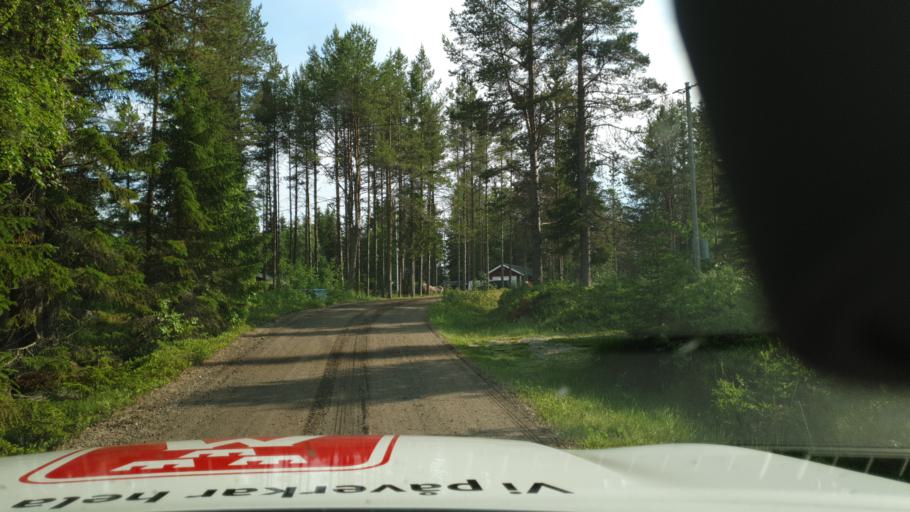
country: SE
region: Vaesterbotten
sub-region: Robertsfors Kommun
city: Robertsfors
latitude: 64.2085
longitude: 21.0772
